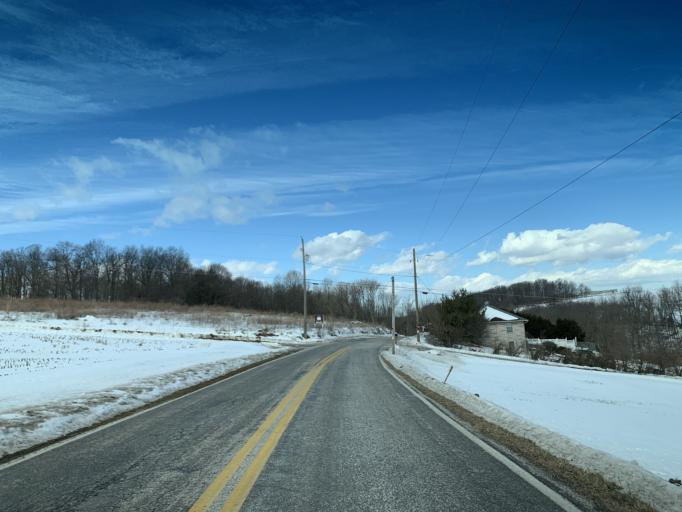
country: US
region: Pennsylvania
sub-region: York County
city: Shrewsbury
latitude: 39.7894
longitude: -76.6475
